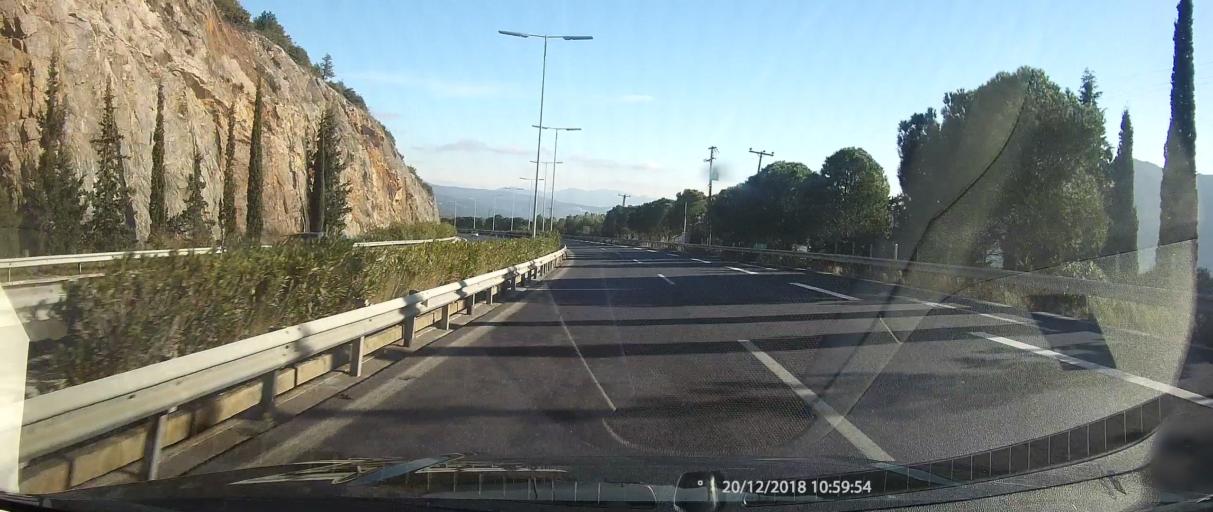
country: GR
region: Peloponnese
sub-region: Nomos Korinthias
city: Nemea
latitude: 37.7037
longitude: 22.5405
